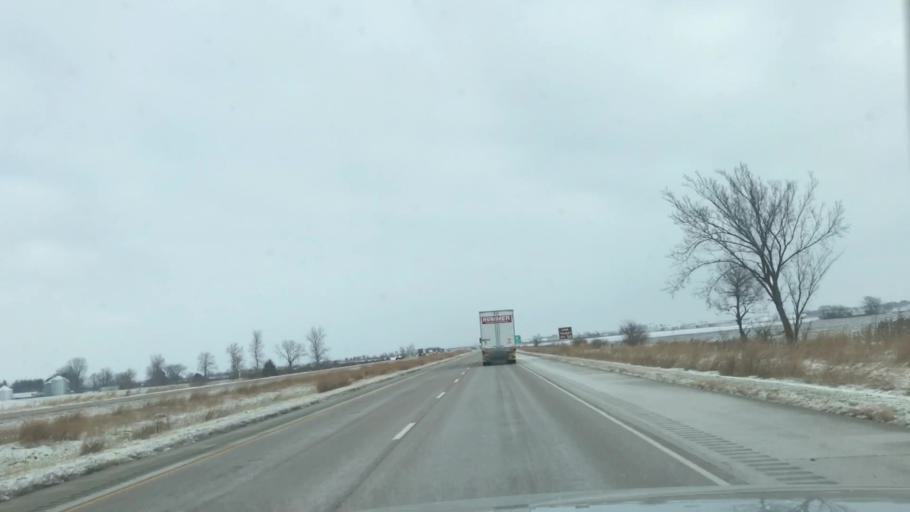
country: US
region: Illinois
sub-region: Montgomery County
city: Litchfield
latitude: 39.1545
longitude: -89.6951
